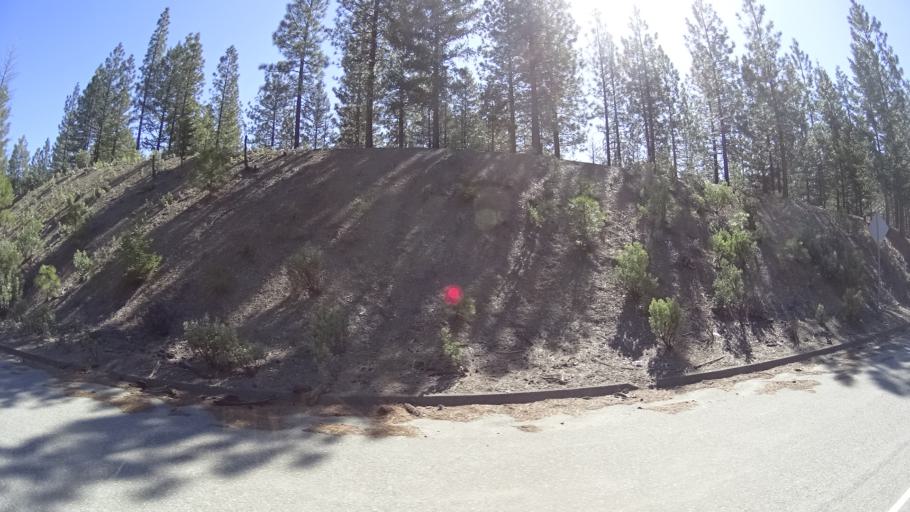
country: US
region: California
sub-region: Tehama County
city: Rancho Tehama Reserve
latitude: 39.6475
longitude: -122.7419
